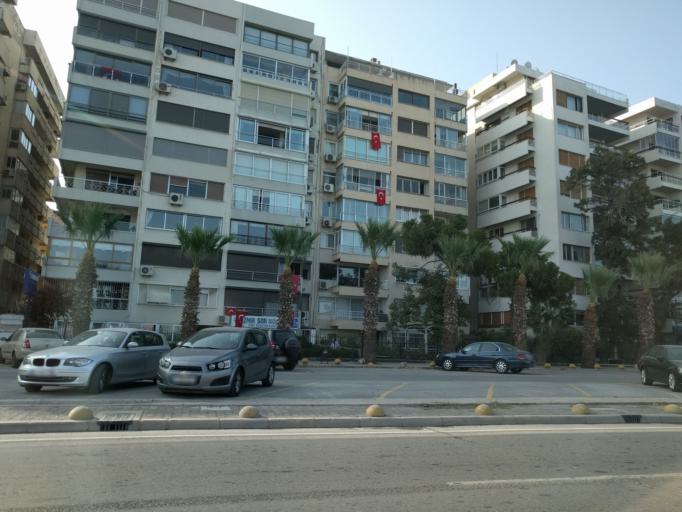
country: TR
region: Izmir
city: Izmir
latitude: 38.4067
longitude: 27.1005
